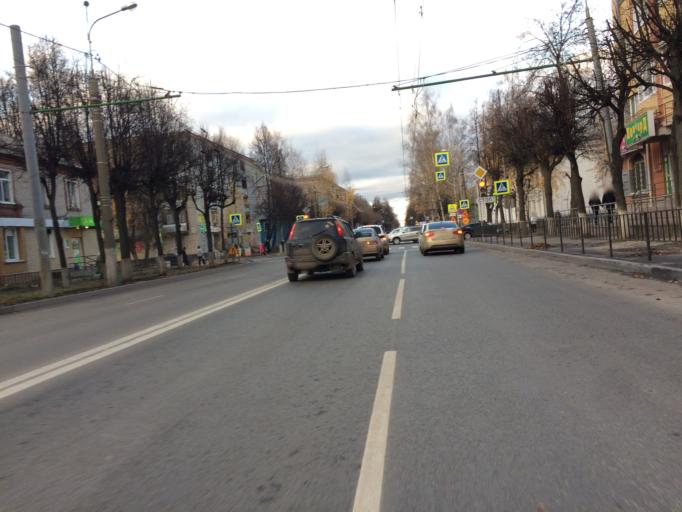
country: RU
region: Mariy-El
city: Yoshkar-Ola
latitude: 56.6434
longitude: 47.8907
